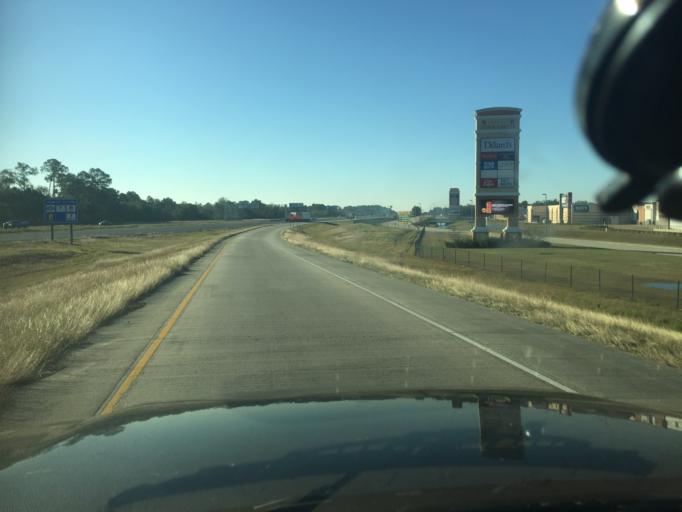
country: US
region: Louisiana
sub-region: Saint Tammany Parish
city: Slidell
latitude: 30.2694
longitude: -89.7562
